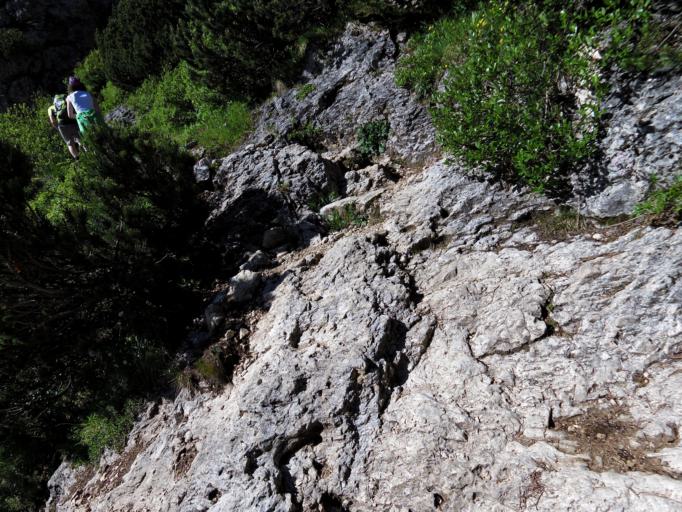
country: IT
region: Trentino-Alto Adige
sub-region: Bolzano
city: Siusi
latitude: 46.5124
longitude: 11.5897
